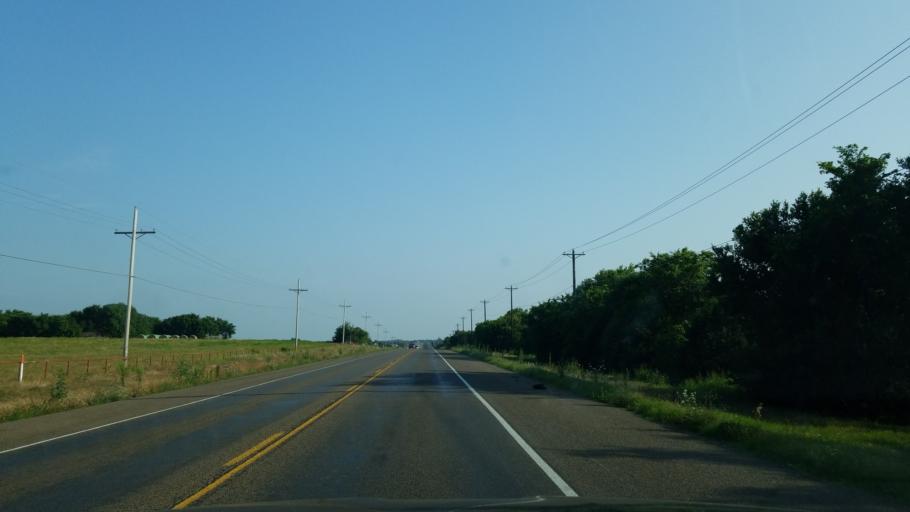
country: US
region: Texas
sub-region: Denton County
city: Pilot Point
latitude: 33.3543
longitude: -96.9668
